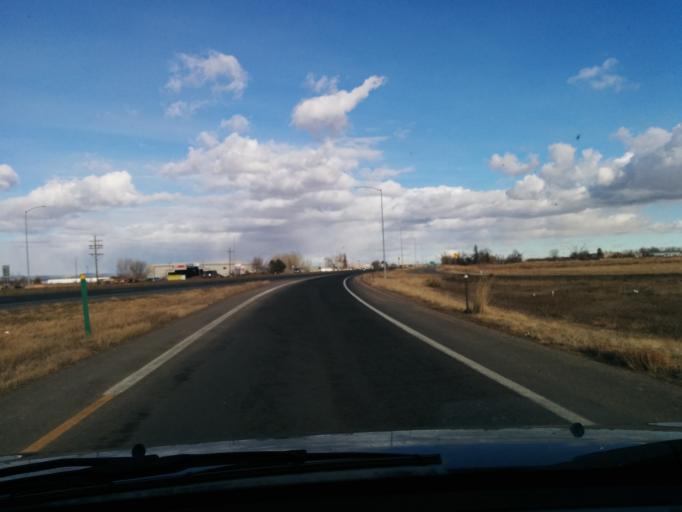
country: US
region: Colorado
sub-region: Larimer County
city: Fort Collins
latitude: 40.5683
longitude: -105.0009
